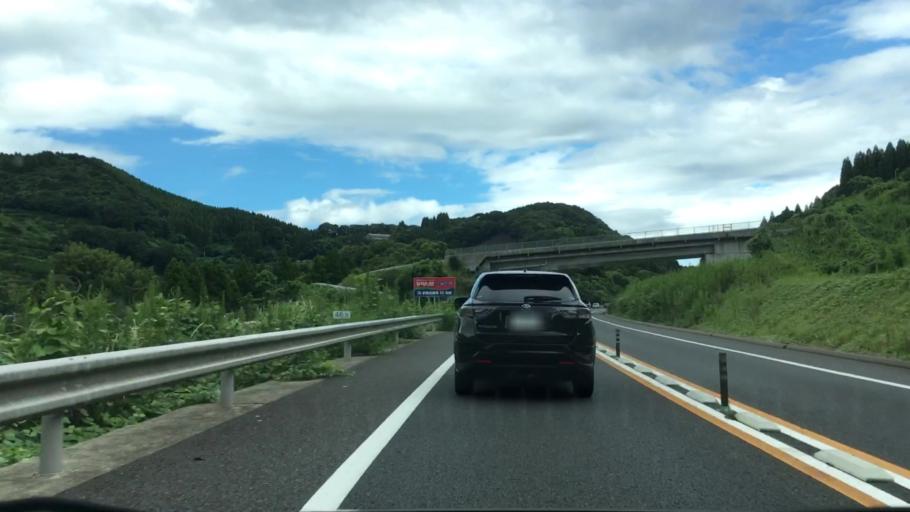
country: JP
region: Saga Prefecture
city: Karatsu
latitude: 33.3960
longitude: 129.9357
